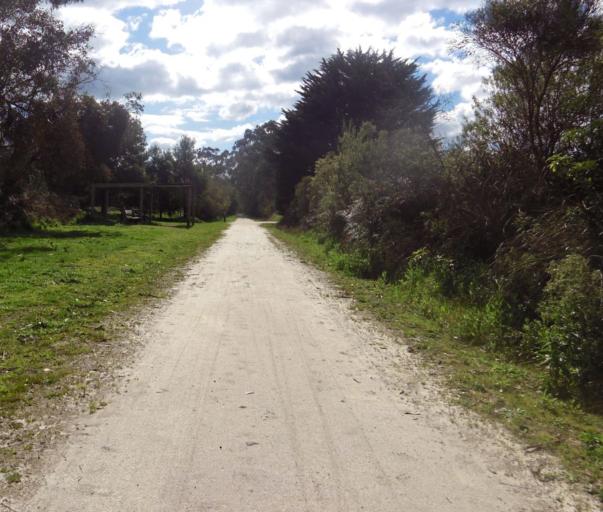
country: AU
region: Victoria
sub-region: Bass Coast
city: North Wonthaggi
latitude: -38.5889
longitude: 146.0392
